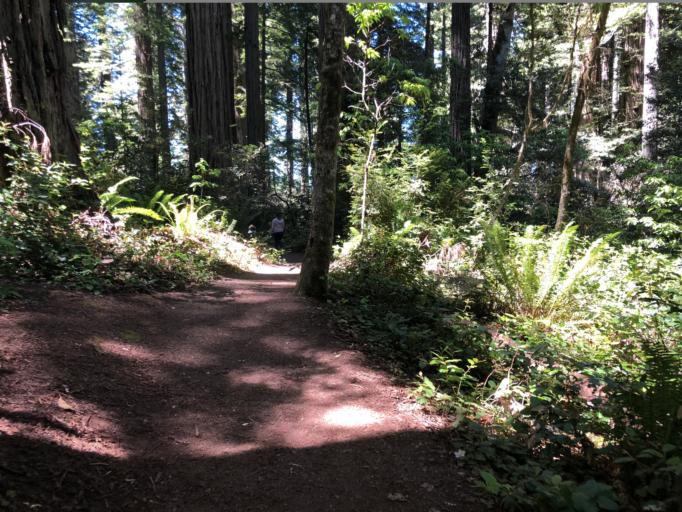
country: US
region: California
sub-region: Humboldt County
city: Westhaven-Moonstone
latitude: 41.3088
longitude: -124.0228
